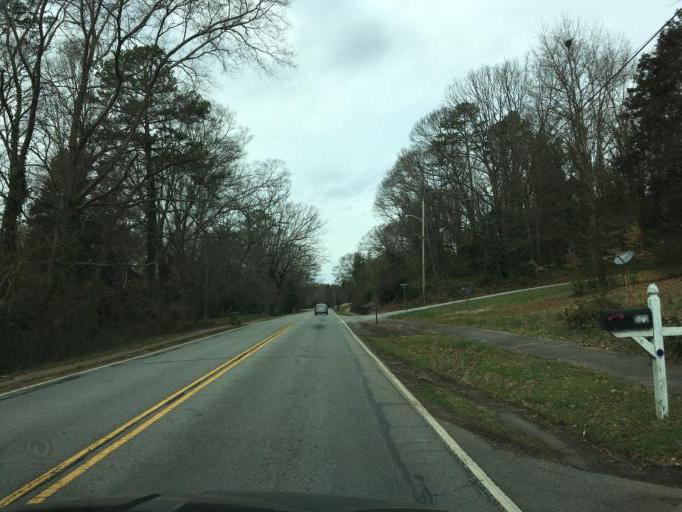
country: US
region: South Carolina
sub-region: Anderson County
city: Pendleton
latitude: 34.6667
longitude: -82.8017
